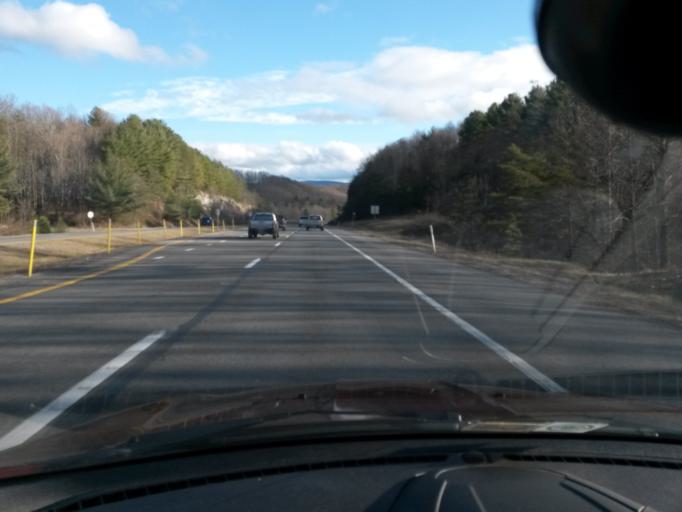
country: US
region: West Virginia
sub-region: Mercer County
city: Athens
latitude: 37.3551
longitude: -81.0206
